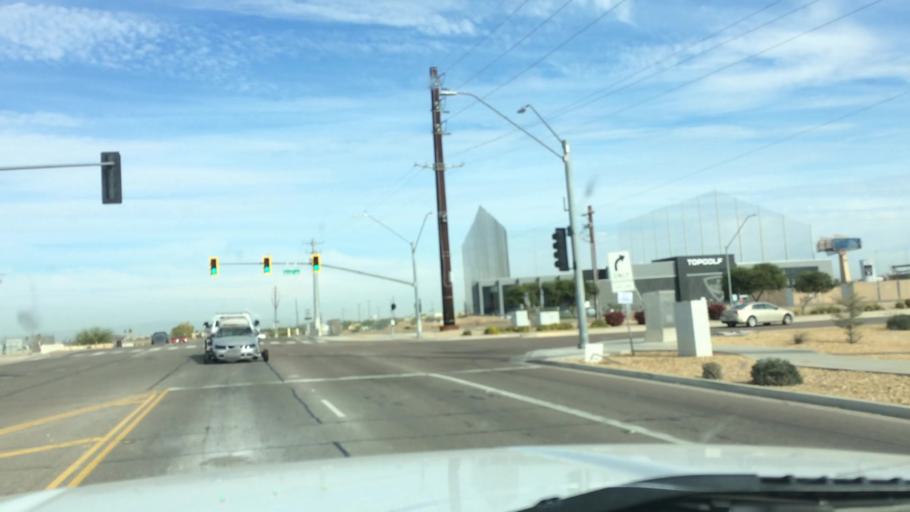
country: US
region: Arizona
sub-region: Maricopa County
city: Peoria
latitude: 33.5221
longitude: -112.2724
